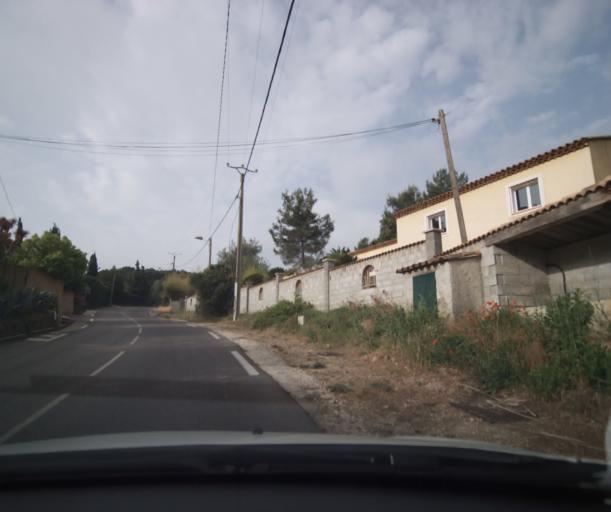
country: FR
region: Provence-Alpes-Cote d'Azur
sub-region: Departement du Var
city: Carqueiranne
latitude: 43.0918
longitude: 6.0607
